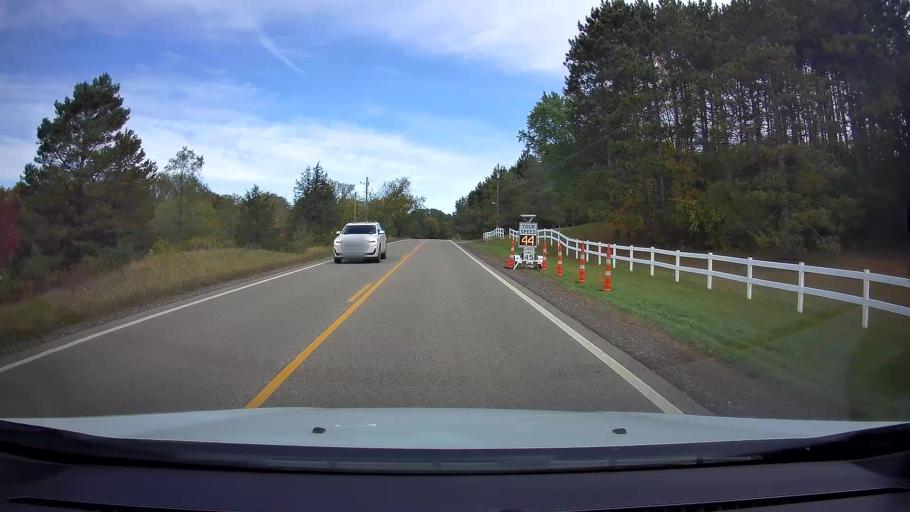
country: US
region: Minnesota
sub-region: Washington County
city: Stillwater
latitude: 45.0866
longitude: -92.8246
